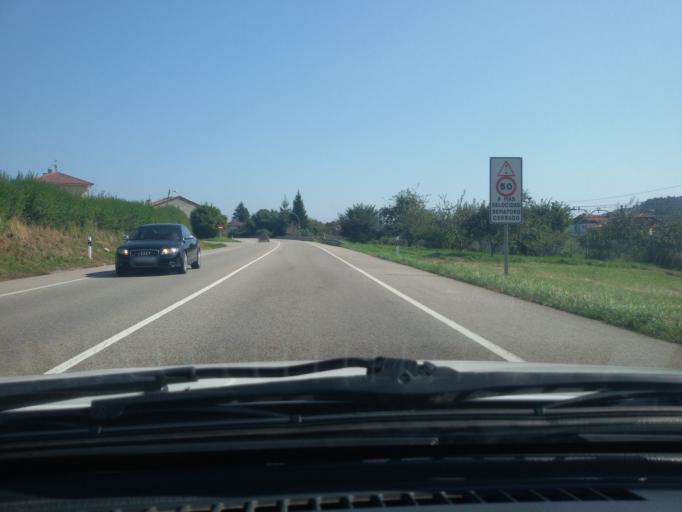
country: ES
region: Asturias
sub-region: Province of Asturias
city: Pola de Siero
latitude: 43.3875
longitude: -5.6790
